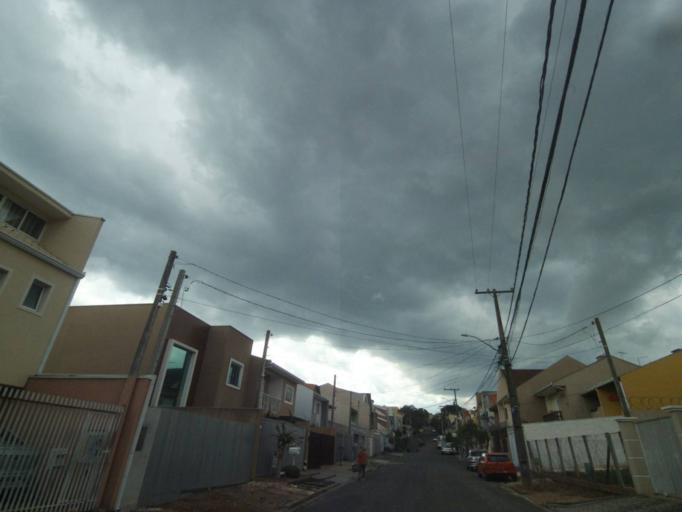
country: BR
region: Parana
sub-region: Curitiba
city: Curitiba
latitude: -25.4515
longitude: -49.3446
